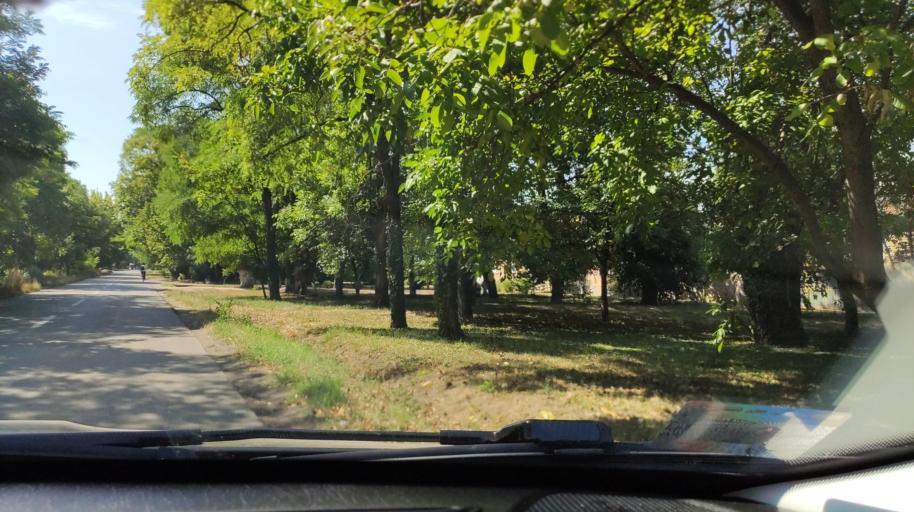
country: RS
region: Autonomna Pokrajina Vojvodina
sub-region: Severnobacki Okrug
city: Backa Topola
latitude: 45.8207
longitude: 19.6440
